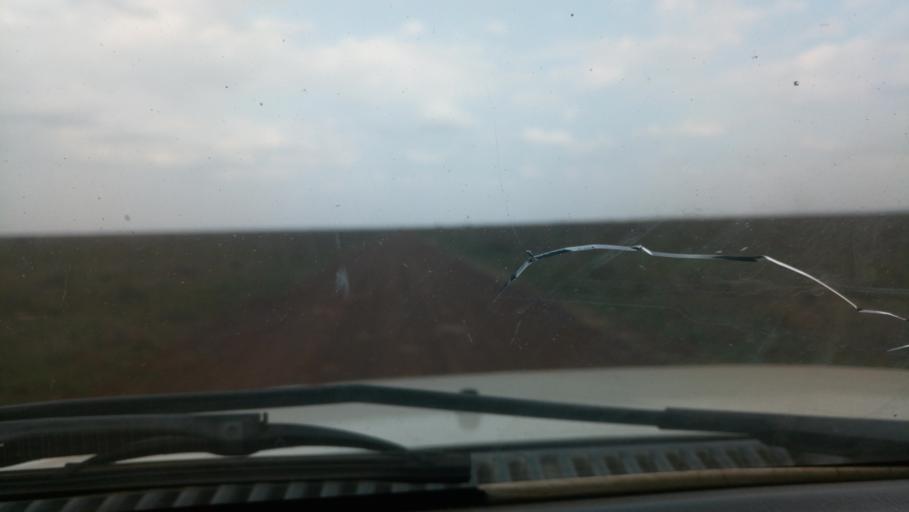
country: KE
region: Nairobi Area
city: Nairobi
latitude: -1.3424
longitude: 36.8218
